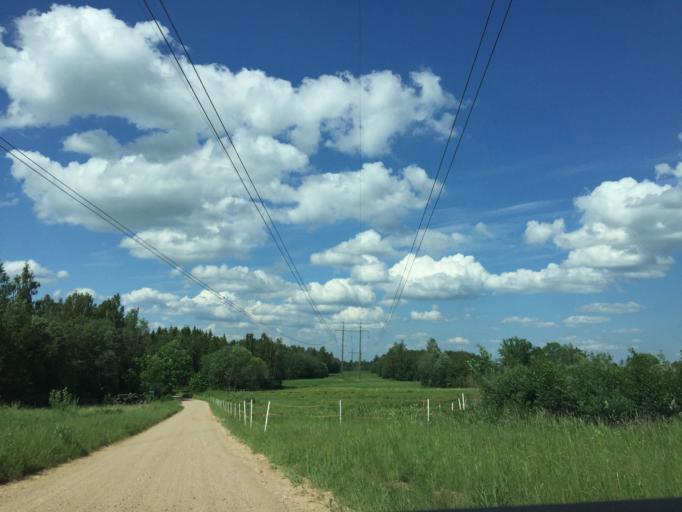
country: LV
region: Priekuli
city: Priekuli
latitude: 57.2444
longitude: 25.4096
